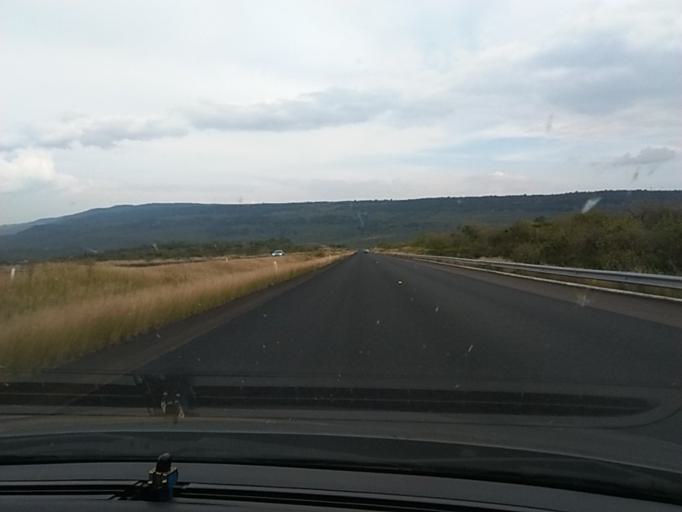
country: MX
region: Mexico
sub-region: Chapultepec
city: Chucandiro
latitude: 19.8766
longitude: -101.4006
